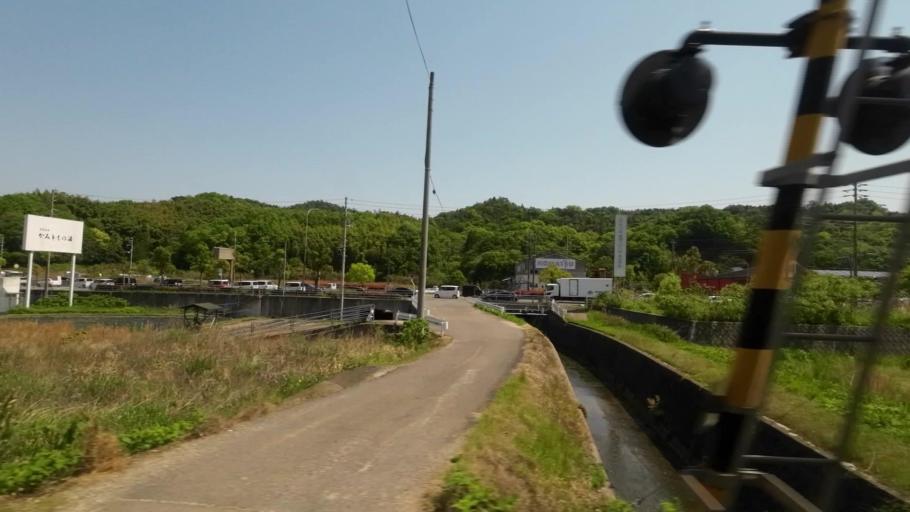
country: JP
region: Ehime
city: Saijo
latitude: 33.9974
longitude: 133.0420
